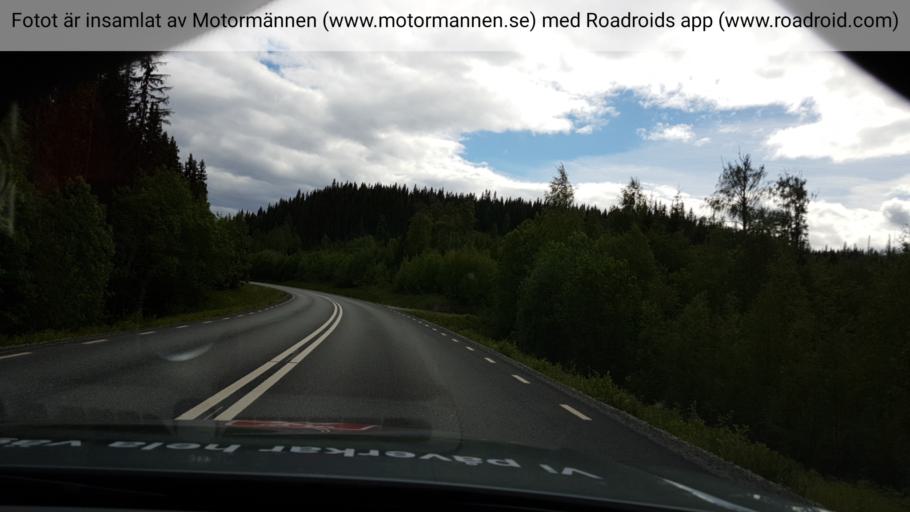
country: SE
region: Jaemtland
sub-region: Stroemsunds Kommun
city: Stroemsund
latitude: 64.0924
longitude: 15.5691
